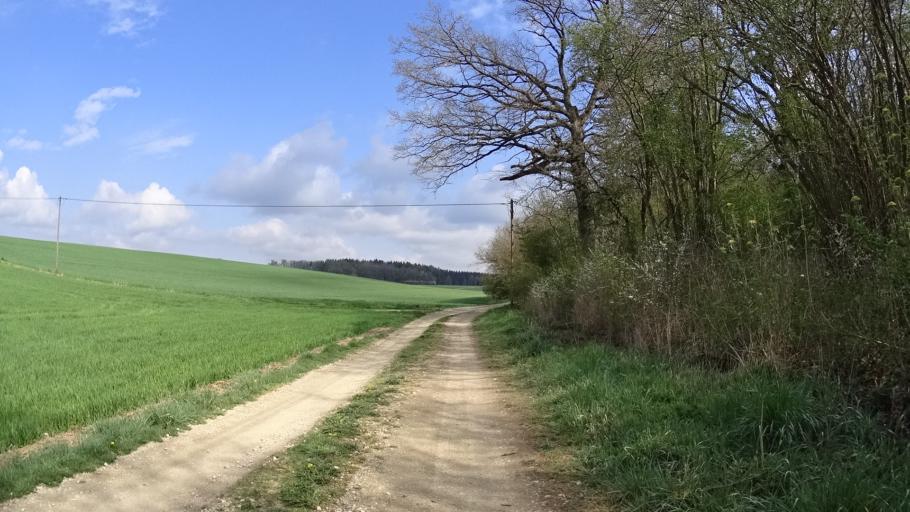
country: DE
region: Bavaria
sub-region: Upper Bavaria
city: Wettstetten
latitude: 48.8424
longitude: 11.4008
